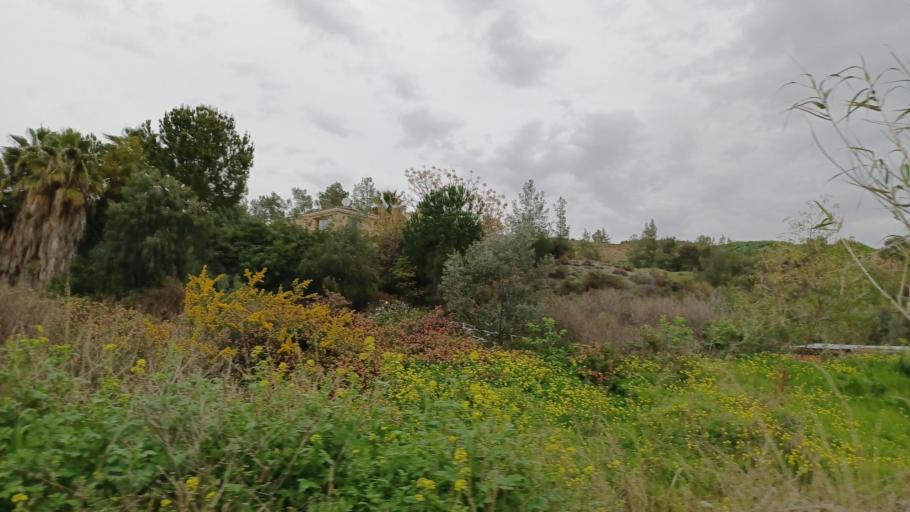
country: CY
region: Pafos
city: Polis
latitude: 35.0571
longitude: 32.4861
